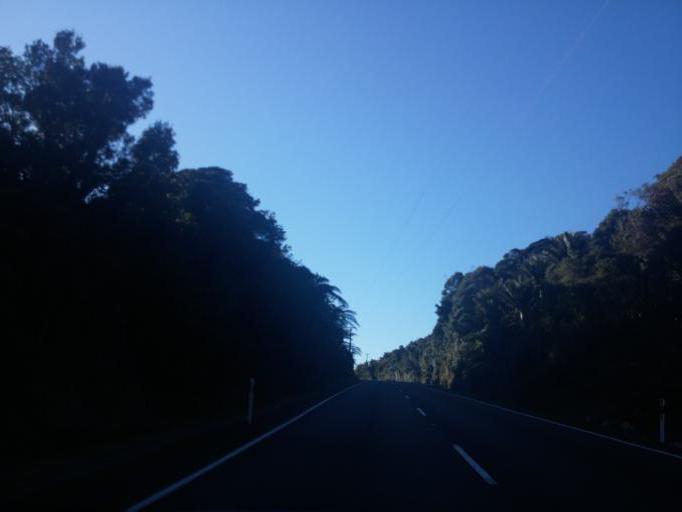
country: NZ
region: West Coast
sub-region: Grey District
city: Greymouth
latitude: -42.0971
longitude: 171.3430
